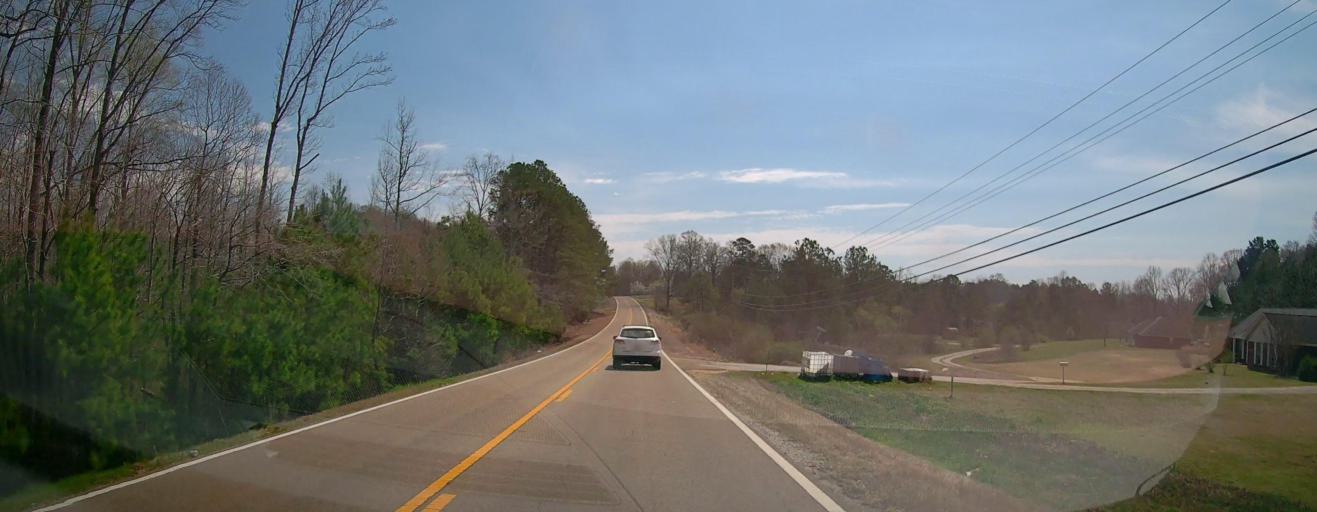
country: US
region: Mississippi
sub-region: Union County
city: New Albany
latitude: 34.4516
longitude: -88.9715
